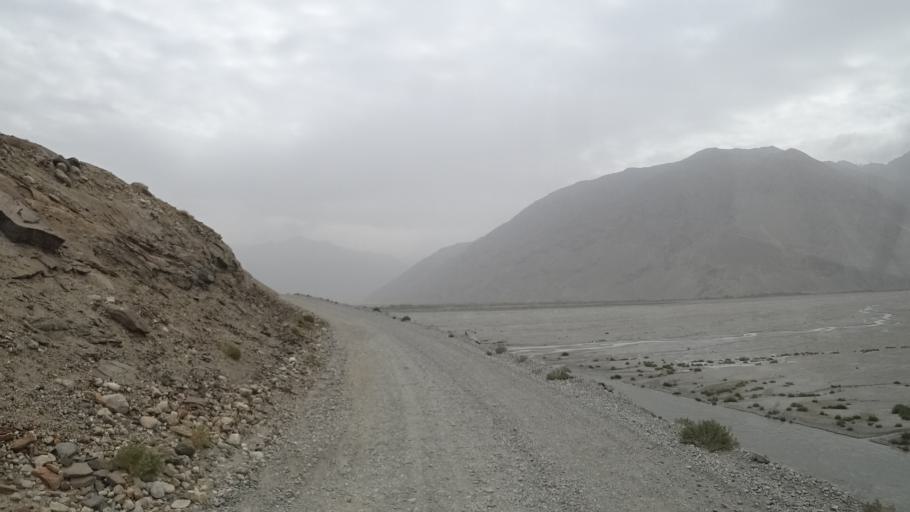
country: AF
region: Badakhshan
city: Khandud
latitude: 37.0031
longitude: 72.5479
